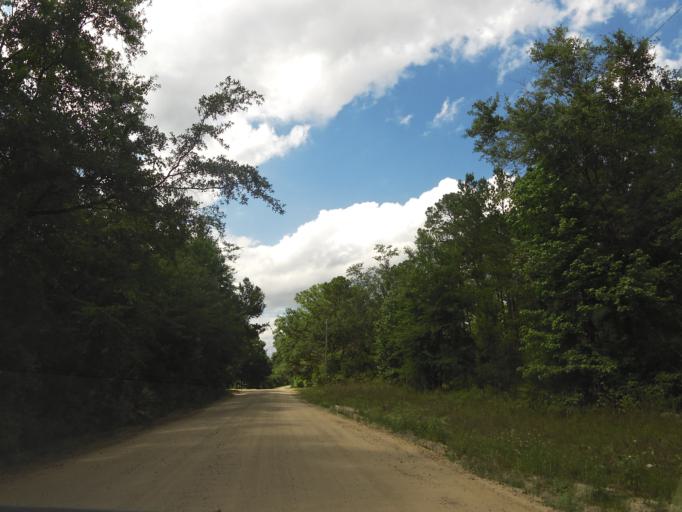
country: US
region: Florida
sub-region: Clay County
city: Asbury Lake
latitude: 29.8936
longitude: -81.8756
